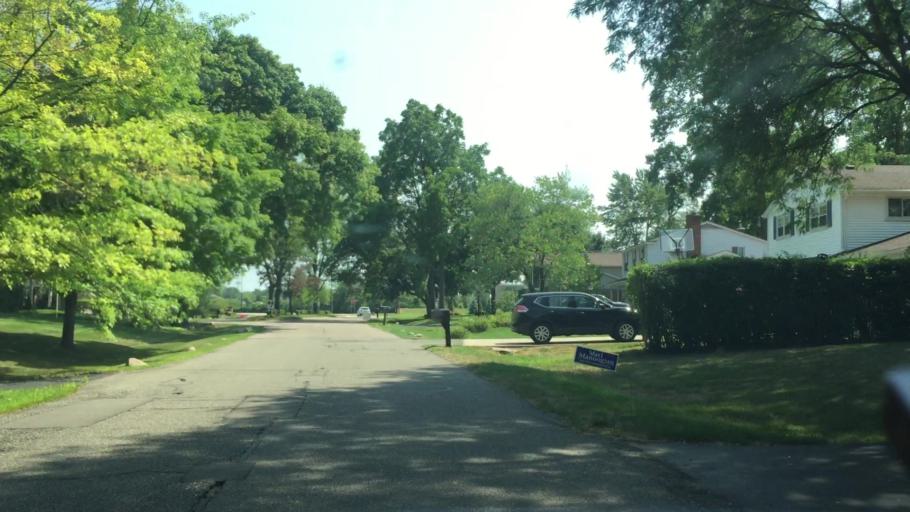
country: US
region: Michigan
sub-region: Oakland County
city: West Bloomfield Township
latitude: 42.5300
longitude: -83.3547
